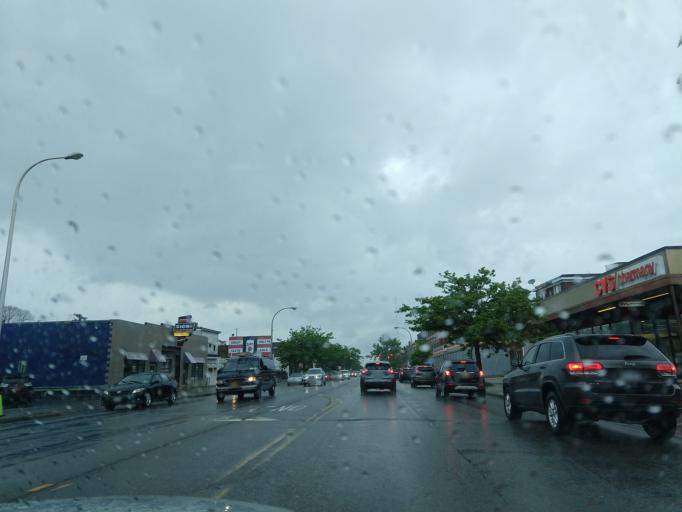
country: US
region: New York
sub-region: Erie County
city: Kenmore
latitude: 42.9408
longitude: -78.8785
